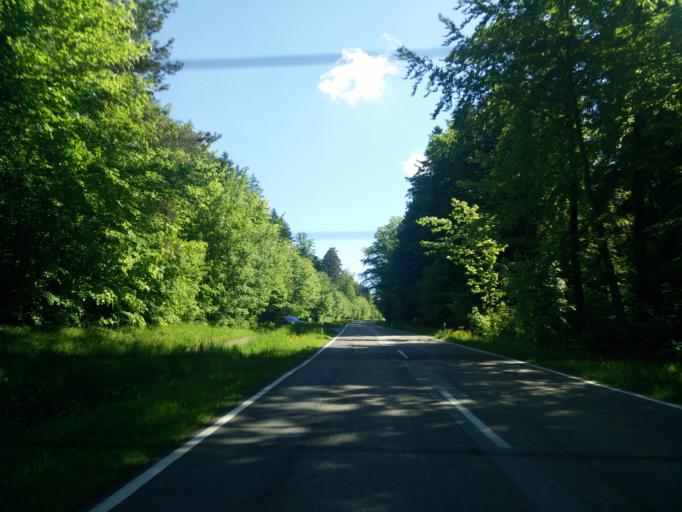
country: DE
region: Baden-Wuerttemberg
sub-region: Regierungsbezirk Stuttgart
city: Gschwend
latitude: 48.9359
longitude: 9.7624
